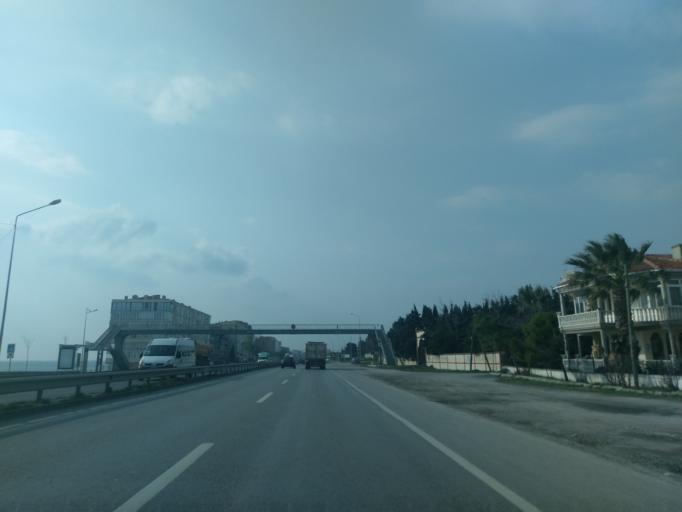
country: TR
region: Istanbul
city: Celaliye
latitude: 41.0453
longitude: 28.4081
